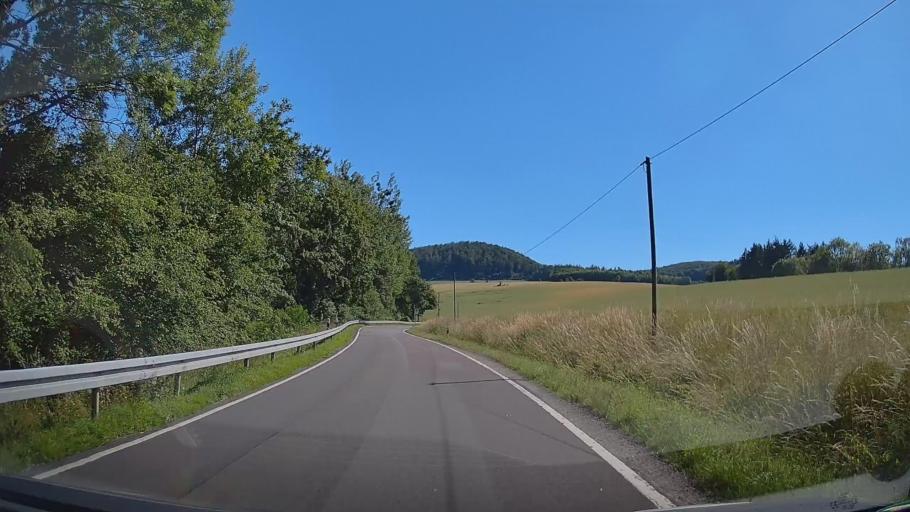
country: DE
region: Lower Saxony
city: Vahlbruch
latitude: 51.9930
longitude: 9.3385
